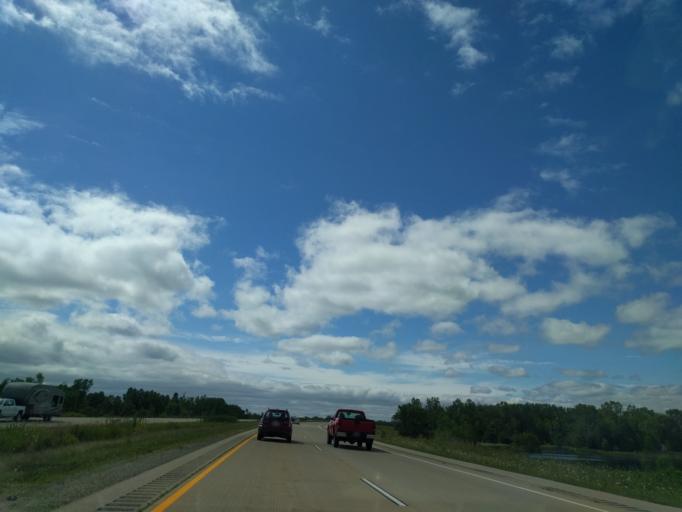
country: US
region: Wisconsin
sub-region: Oconto County
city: Oconto
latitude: 44.9102
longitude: -87.8804
